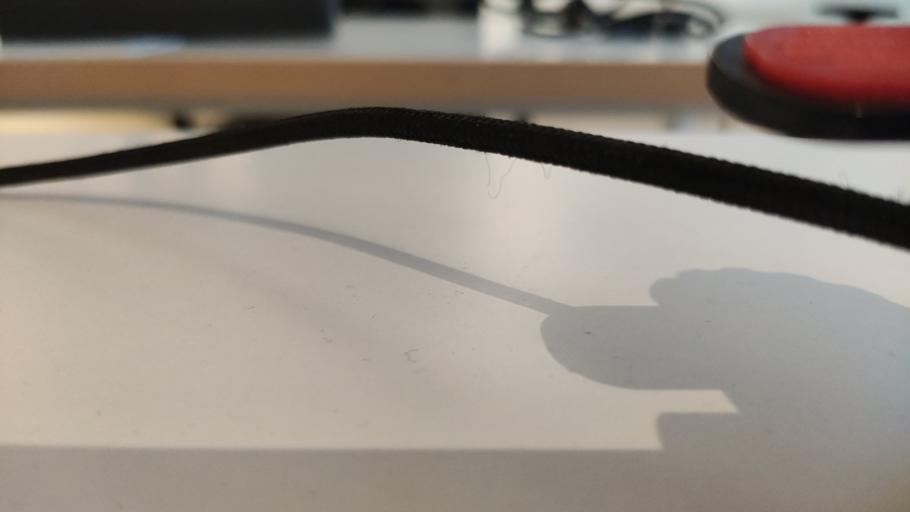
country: RU
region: Moskovskaya
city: Sychevo
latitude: 55.8447
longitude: 36.3394
